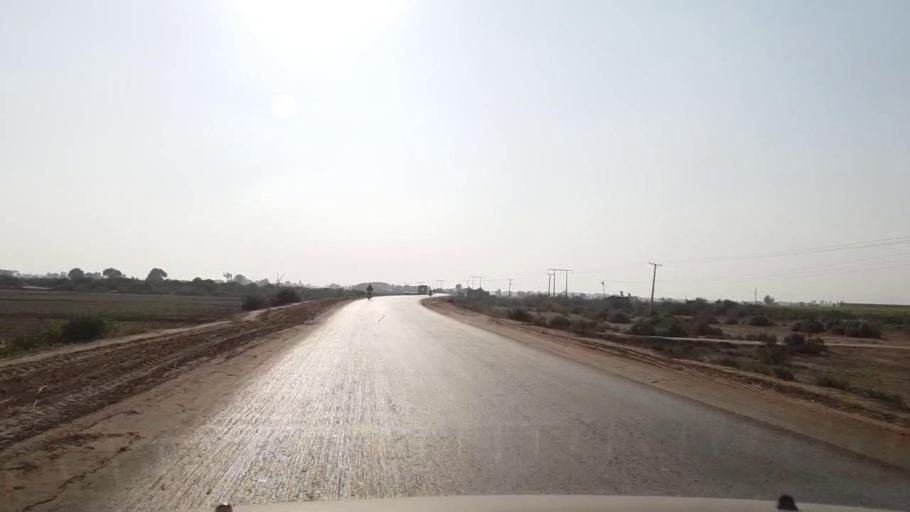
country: PK
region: Sindh
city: Tando Muhammad Khan
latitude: 25.0224
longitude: 68.4153
